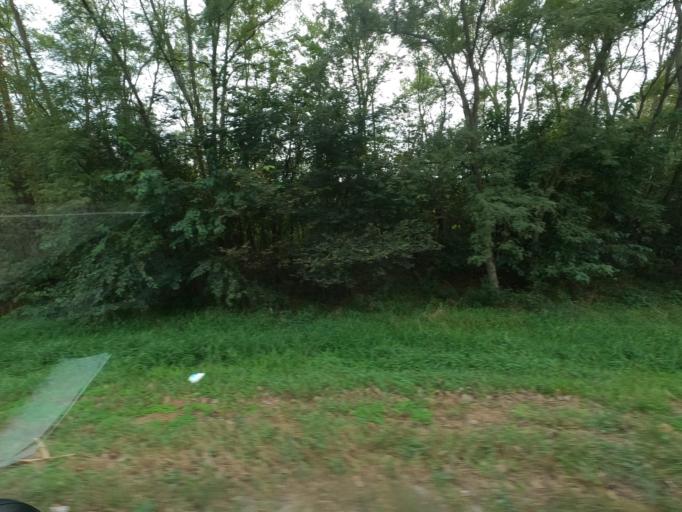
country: US
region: Iowa
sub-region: Jefferson County
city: Fairfield
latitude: 40.8907
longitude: -92.1747
